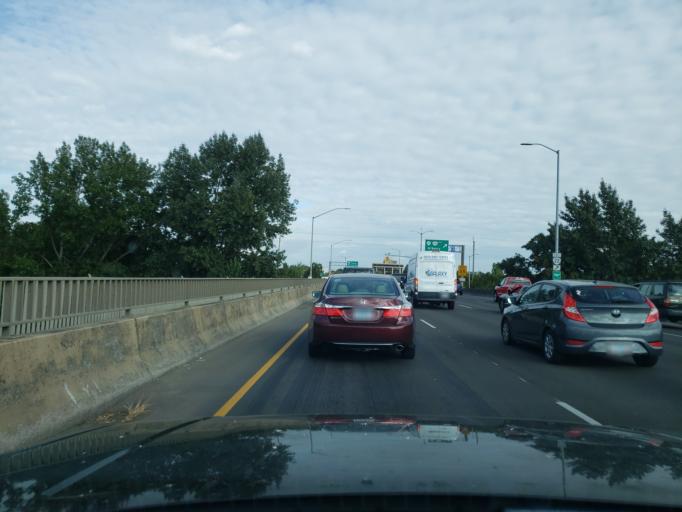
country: US
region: Oregon
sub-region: Marion County
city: Salem
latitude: 44.9448
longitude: -123.0427
